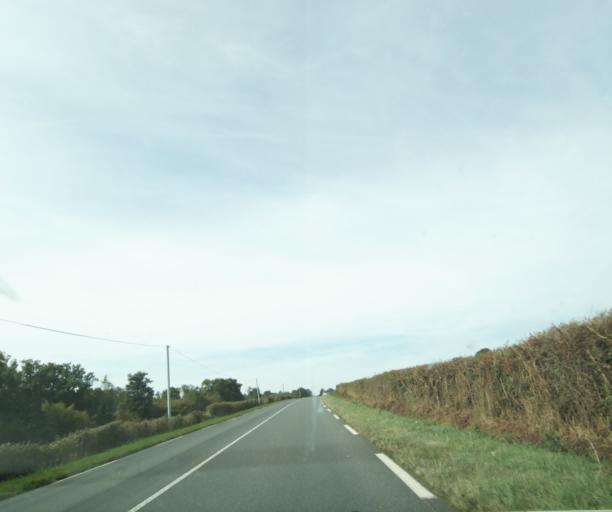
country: FR
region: Auvergne
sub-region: Departement de l'Allier
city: Le Donjon
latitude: 46.3430
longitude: 3.7825
